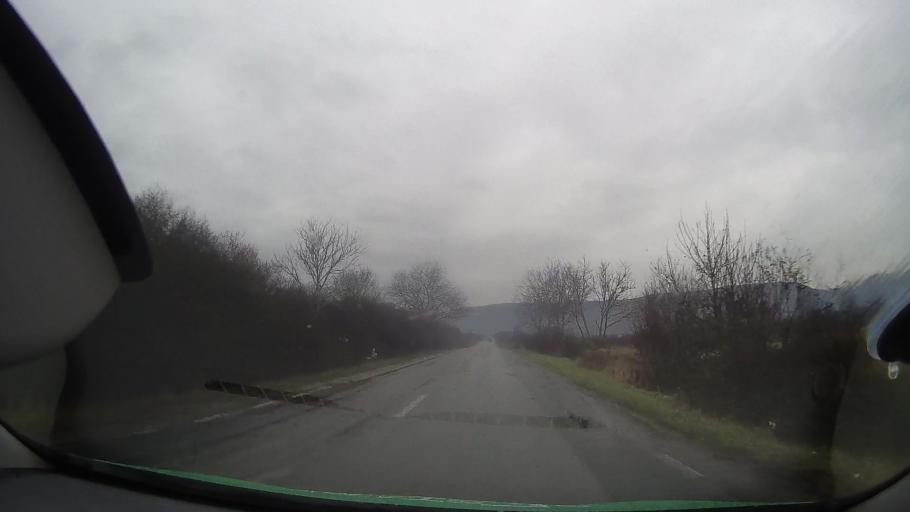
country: RO
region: Bihor
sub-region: Comuna Sambata
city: Sambata
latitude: 46.7795
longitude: 22.1876
